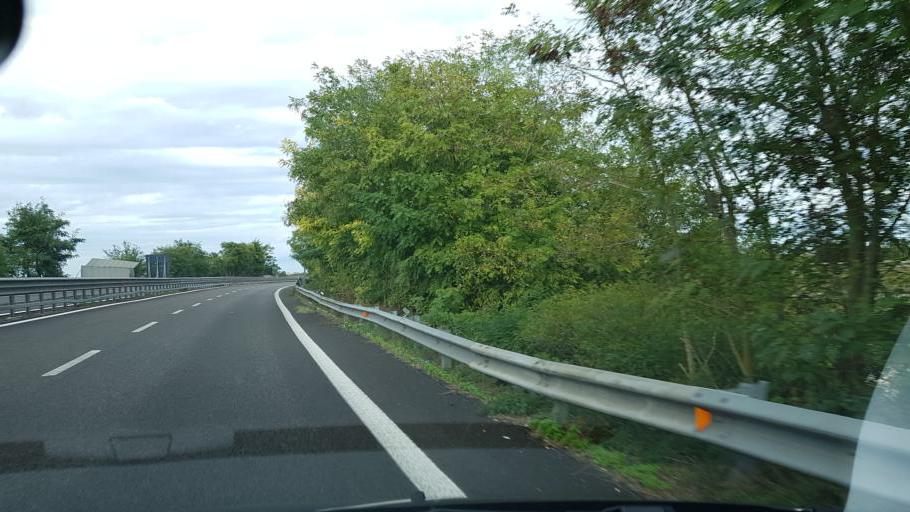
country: IT
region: Apulia
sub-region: Provincia di Lecce
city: Castromediano
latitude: 40.3270
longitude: 18.1856
